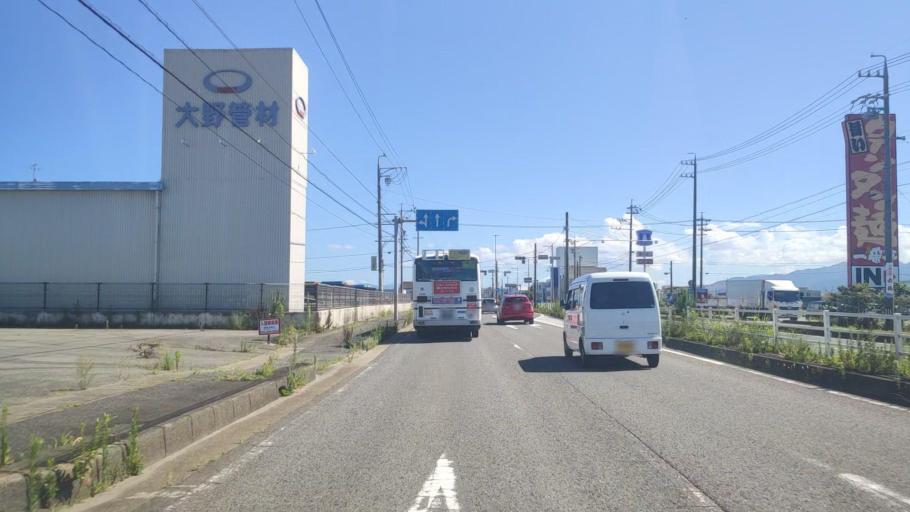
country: JP
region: Mie
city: Hisai-motomachi
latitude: 34.6413
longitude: 136.5184
